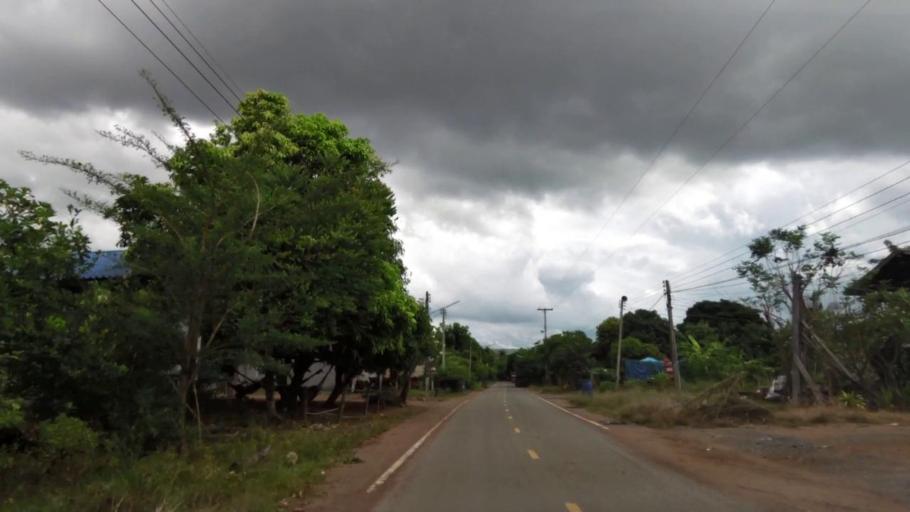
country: TH
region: Nakhon Sawan
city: Phai Sali
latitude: 15.6054
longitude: 100.6558
